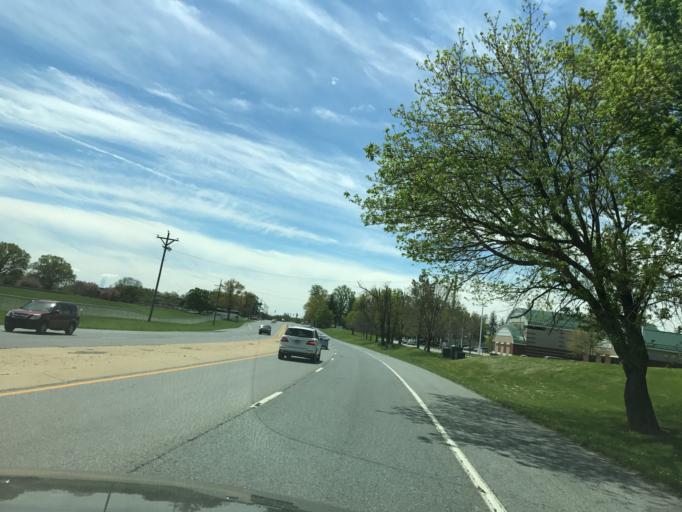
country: US
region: Delaware
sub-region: New Castle County
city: Elsmere
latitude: 39.7539
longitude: -75.6093
